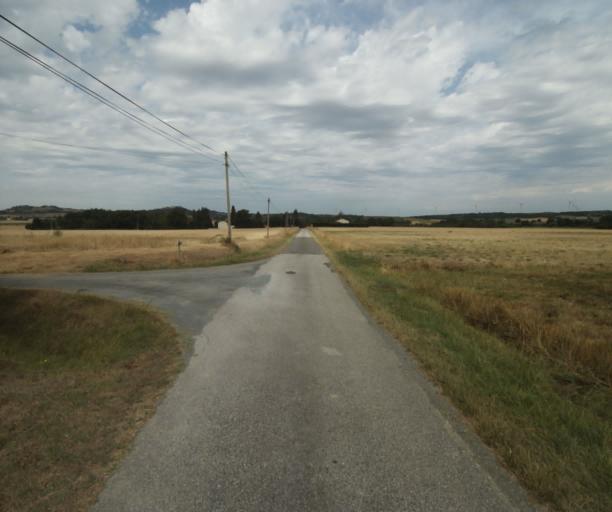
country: FR
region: Midi-Pyrenees
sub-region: Departement de la Haute-Garonne
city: Saint-Felix-Lauragais
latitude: 43.4399
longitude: 1.9305
